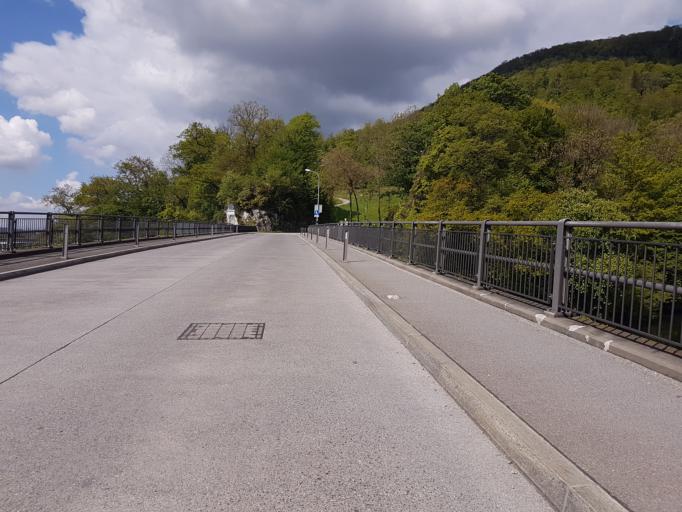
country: CH
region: Aargau
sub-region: Bezirk Zofingen
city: Aarburg
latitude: 47.3204
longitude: 7.8985
